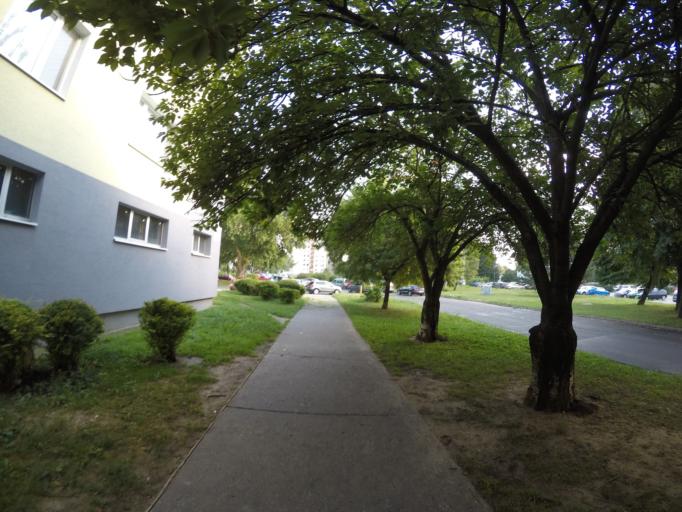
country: SK
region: Bratislavsky
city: Bratislava
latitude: 48.1187
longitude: 17.1056
